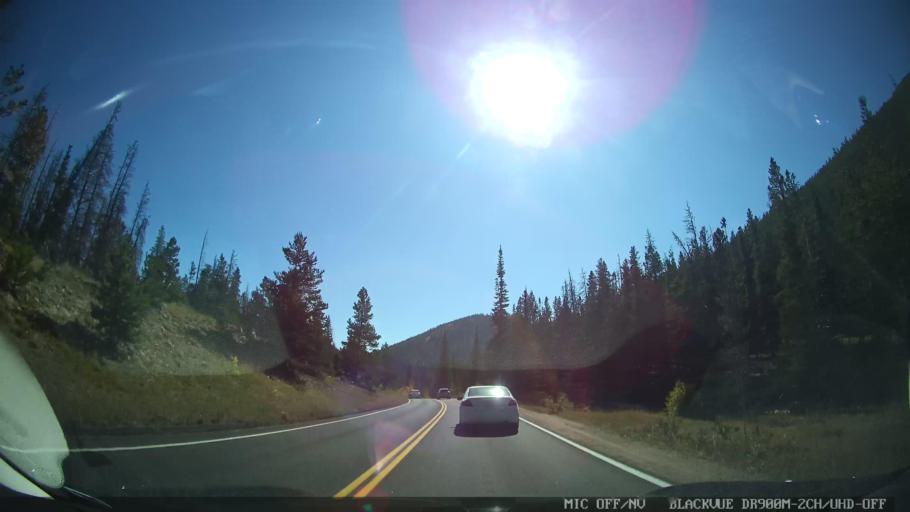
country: US
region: Colorado
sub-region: Larimer County
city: Estes Park
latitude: 40.3956
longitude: -105.6327
